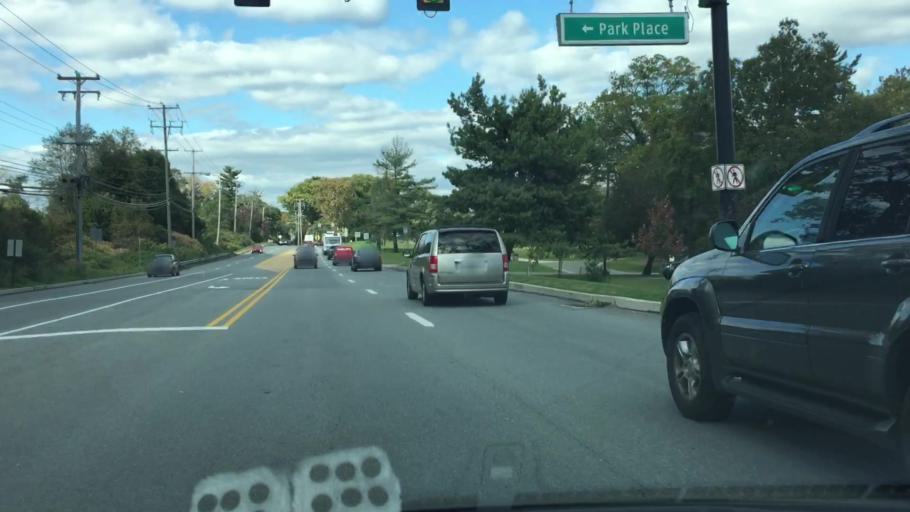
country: US
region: Pennsylvania
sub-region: Delaware County
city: Media
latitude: 39.9402
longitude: -75.3950
